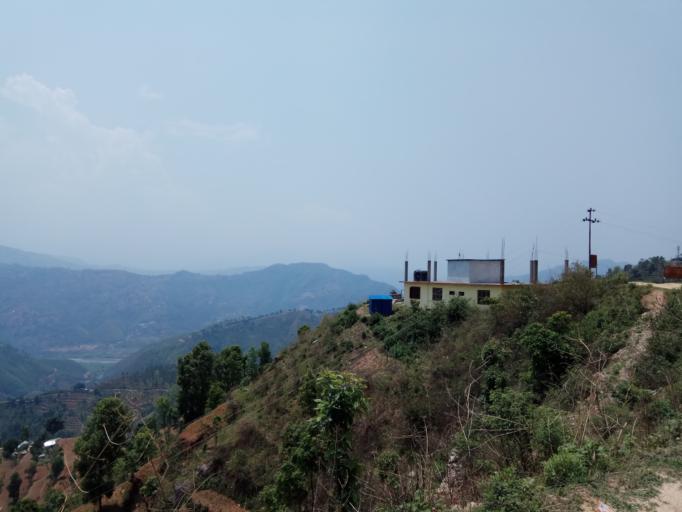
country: NP
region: Central Region
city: Kirtipur
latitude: 27.8958
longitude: 85.0697
